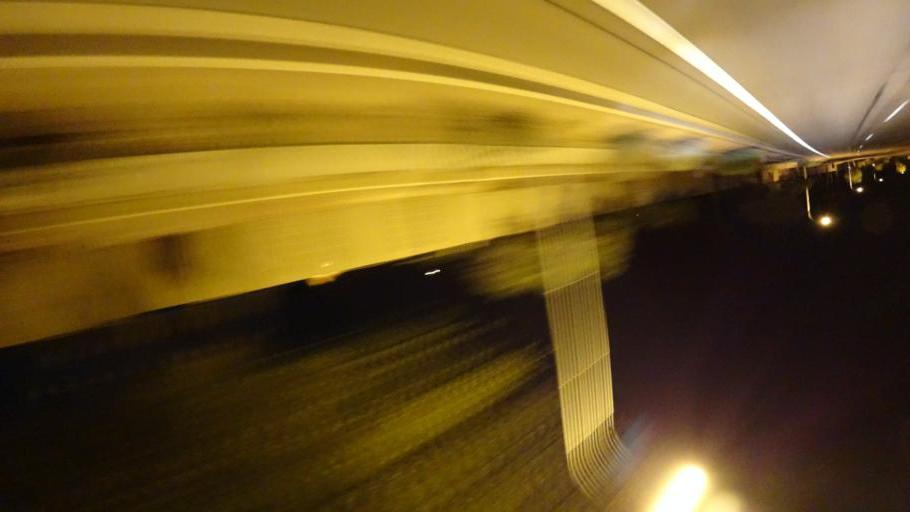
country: US
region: Arizona
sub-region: Maricopa County
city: Guadalupe
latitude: 33.3446
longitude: -111.9931
